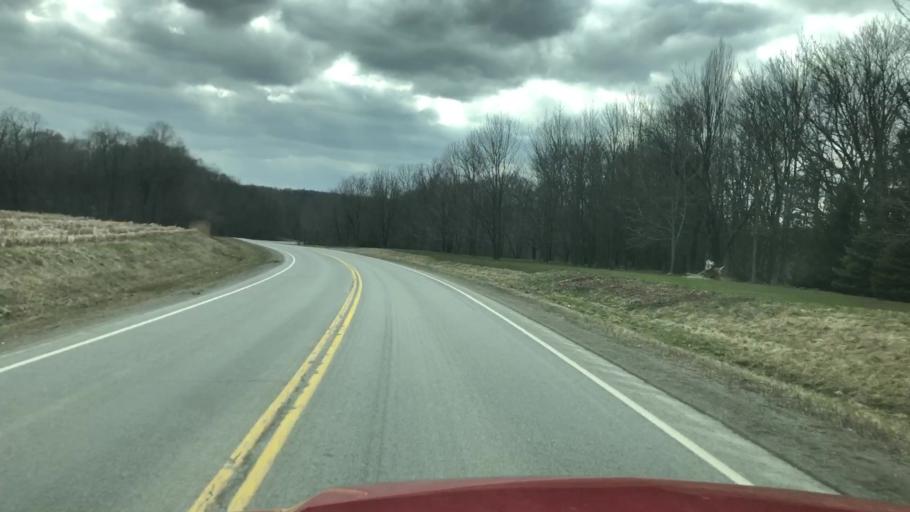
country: US
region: New York
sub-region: Monroe County
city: Fairport
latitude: 43.1307
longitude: -77.3641
